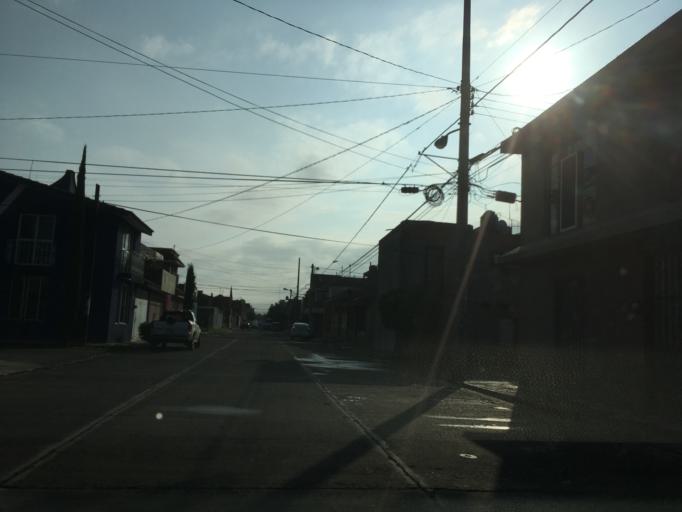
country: MX
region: Michoacan
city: Morelia
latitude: 19.6927
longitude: -101.2207
